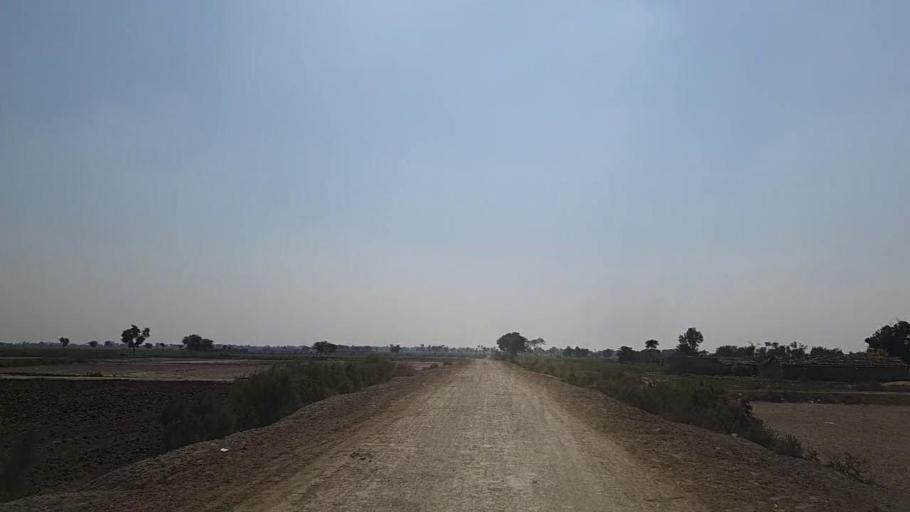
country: PK
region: Sindh
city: Daur
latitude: 26.4557
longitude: 68.2708
